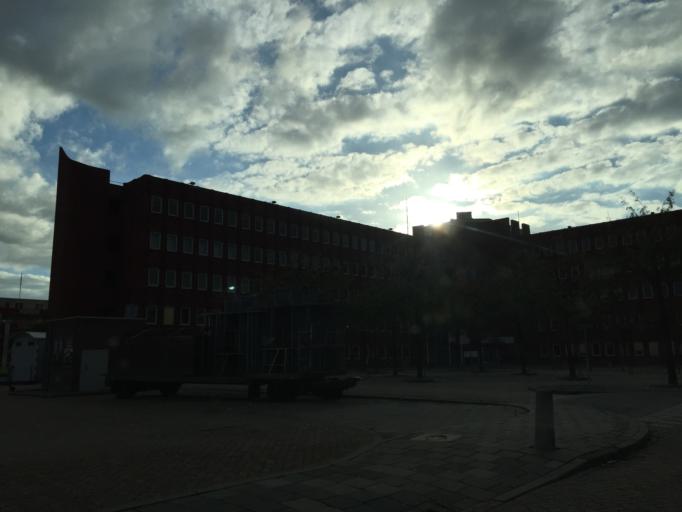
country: NL
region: Utrecht
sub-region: Gemeente Nieuwegein
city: Nieuwegein
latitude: 52.0288
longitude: 5.0768
